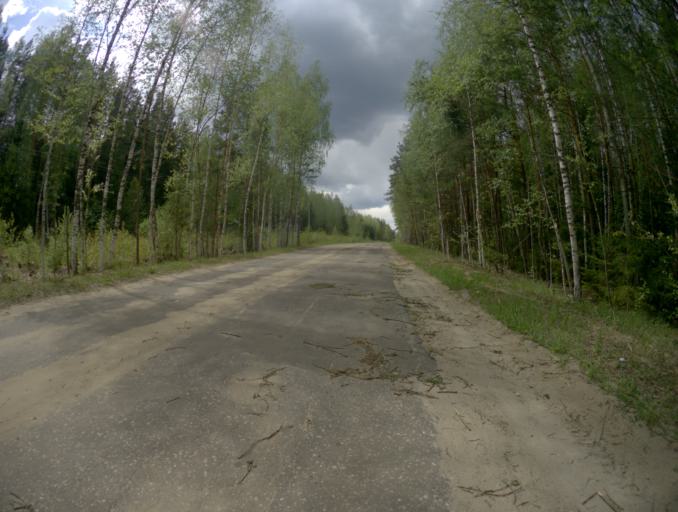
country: RU
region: Vladimir
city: Velikodvorskiy
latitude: 55.2432
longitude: 40.7404
